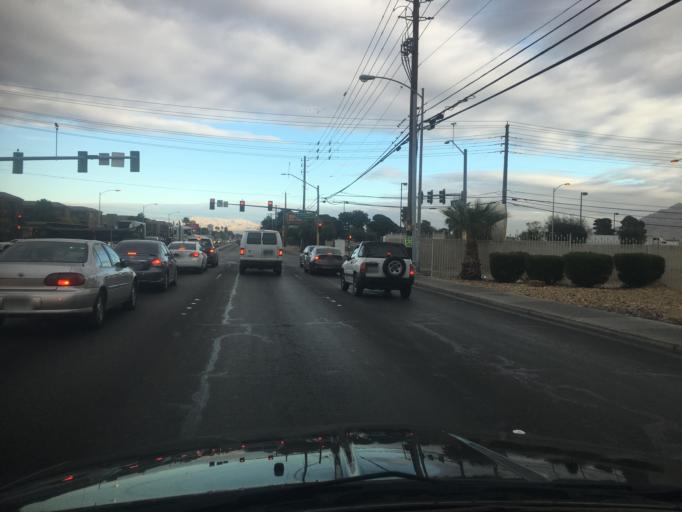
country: US
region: Nevada
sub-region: Clark County
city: Whitney
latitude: 36.1144
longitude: -115.0646
